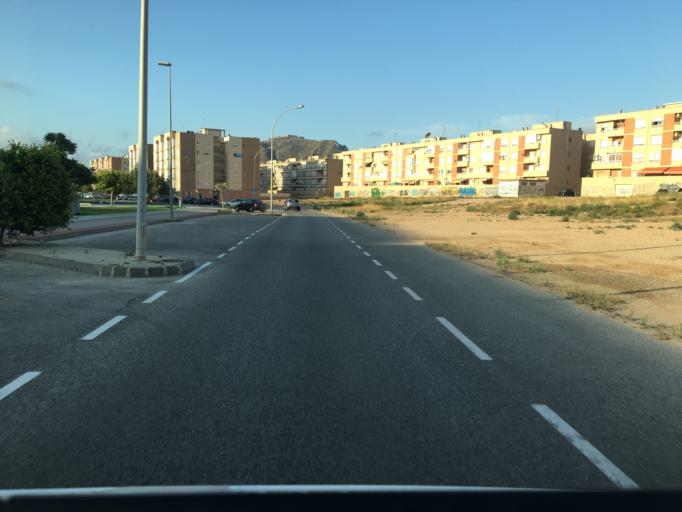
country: ES
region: Murcia
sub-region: Murcia
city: Cartagena
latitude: 37.6236
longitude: -1.0054
